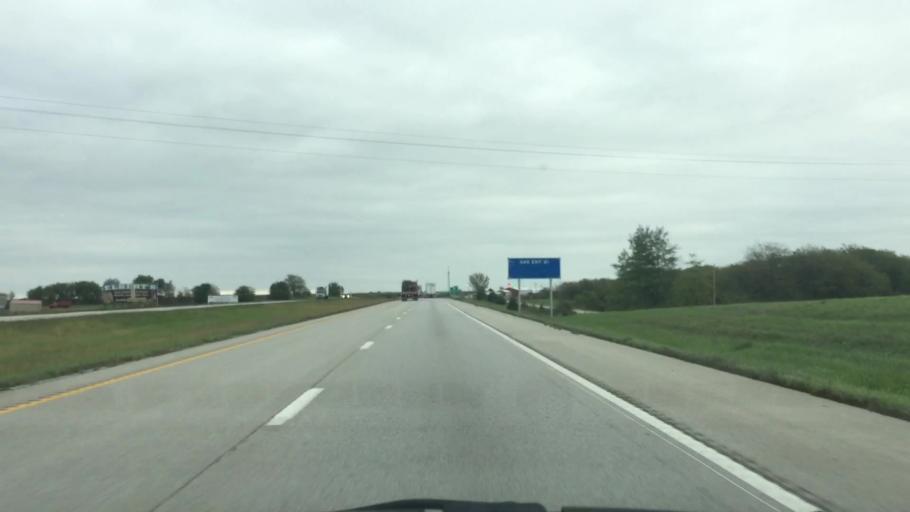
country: US
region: Missouri
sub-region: Clinton County
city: Cameron
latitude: 39.8459
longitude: -94.1799
